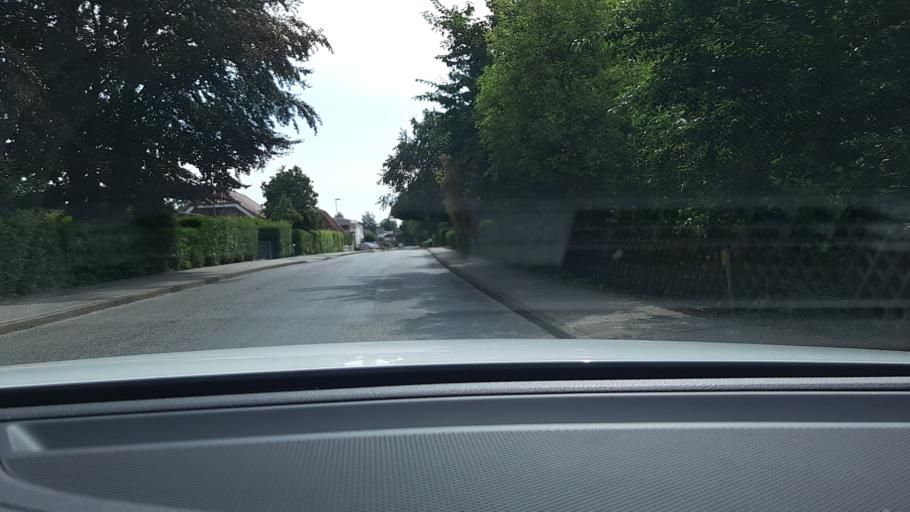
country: DE
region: Schleswig-Holstein
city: Zarpen
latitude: 53.8750
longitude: 10.5191
